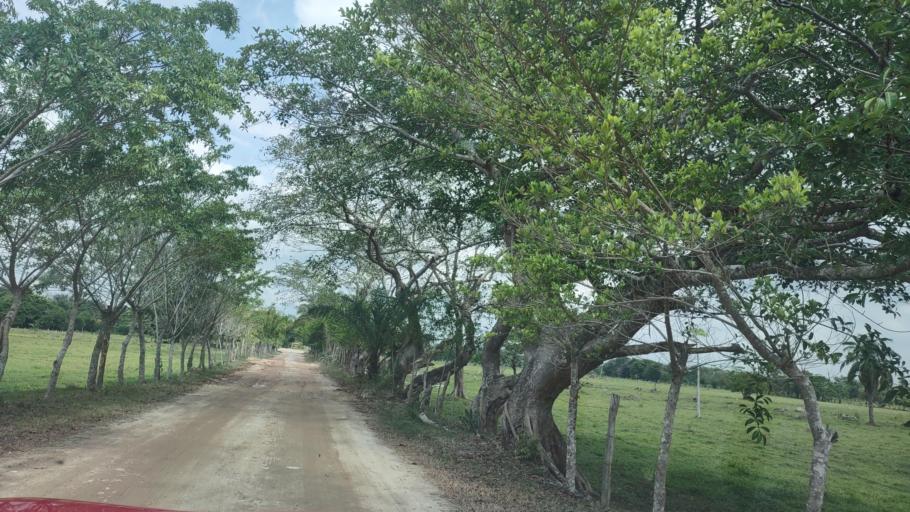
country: MX
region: Veracruz
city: Las Choapas
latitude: 17.9608
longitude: -94.1209
